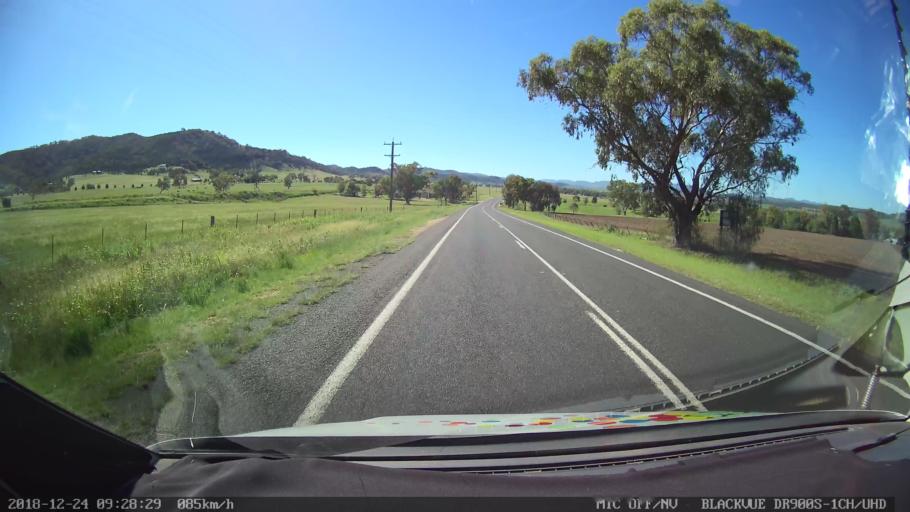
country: AU
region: New South Wales
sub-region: Liverpool Plains
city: Quirindi
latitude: -31.5384
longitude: 150.6892
